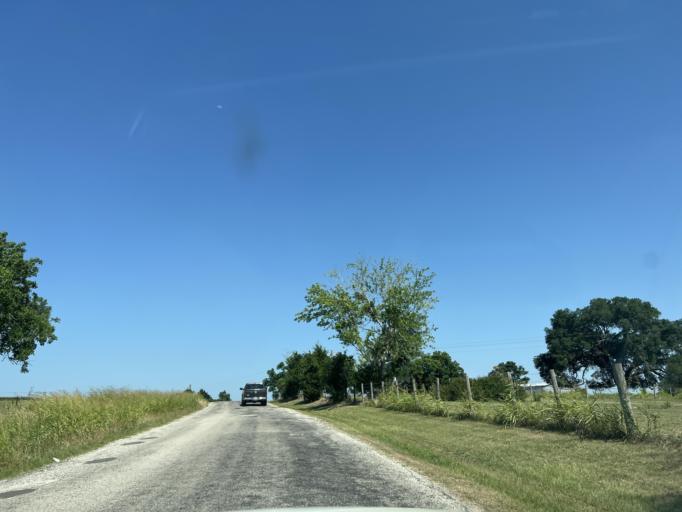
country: US
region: Texas
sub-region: Washington County
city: Brenham
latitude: 30.1634
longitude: -96.3274
